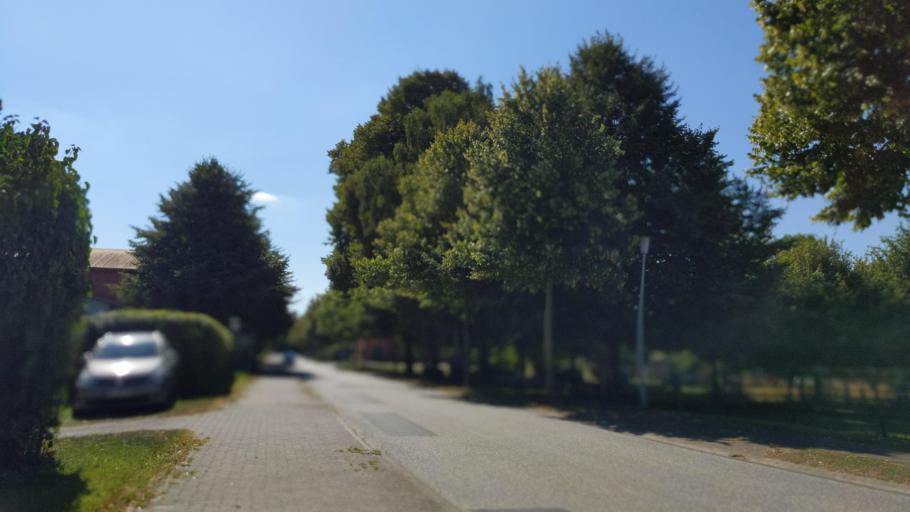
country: DE
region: Mecklenburg-Vorpommern
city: Selmsdorf
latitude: 53.8297
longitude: 10.8885
